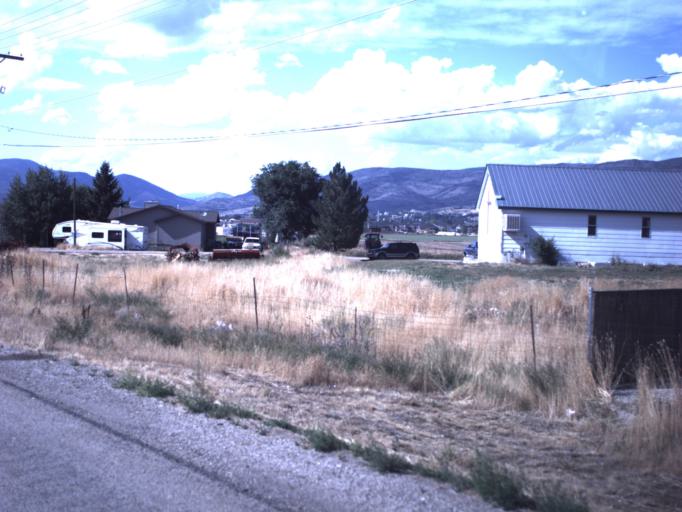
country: US
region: Utah
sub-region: Wasatch County
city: Heber
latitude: 40.4847
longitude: -111.4048
